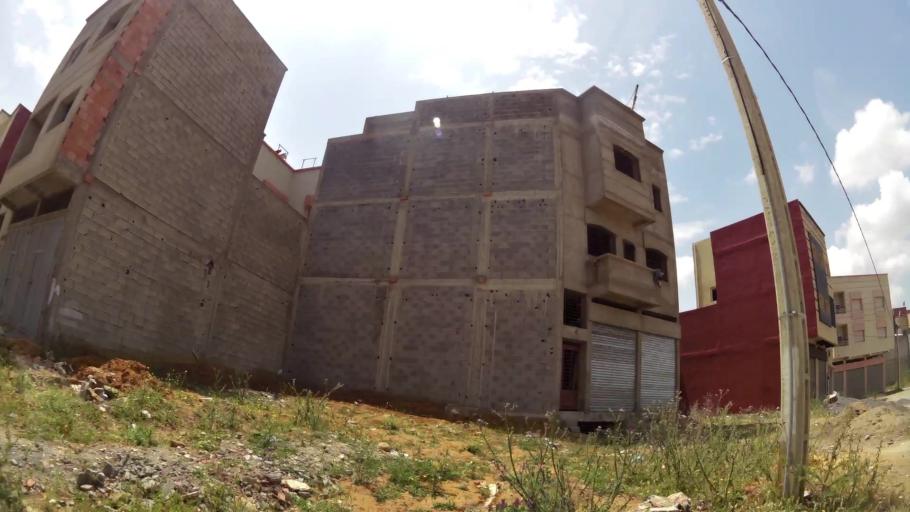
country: MA
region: Gharb-Chrarda-Beni Hssen
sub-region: Kenitra Province
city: Kenitra
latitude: 34.0106
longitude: -6.5379
